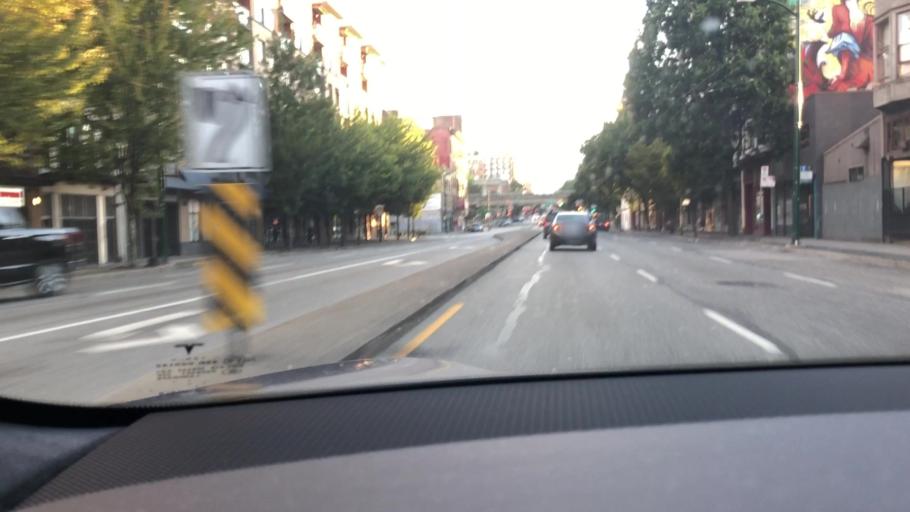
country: CA
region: British Columbia
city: Vancouver
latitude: 49.2751
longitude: -123.0999
